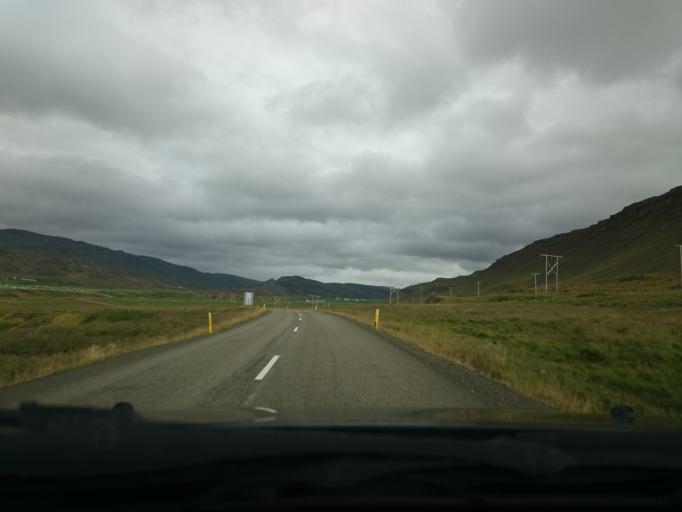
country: IS
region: West
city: Stykkisholmur
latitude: 65.4604
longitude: -21.9144
